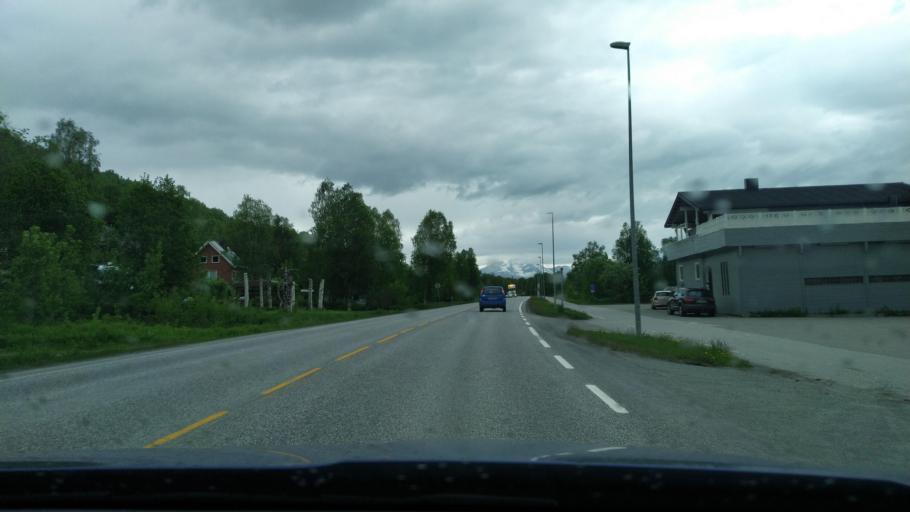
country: NO
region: Troms
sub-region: Malselv
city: Moen
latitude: 69.0315
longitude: 18.5026
